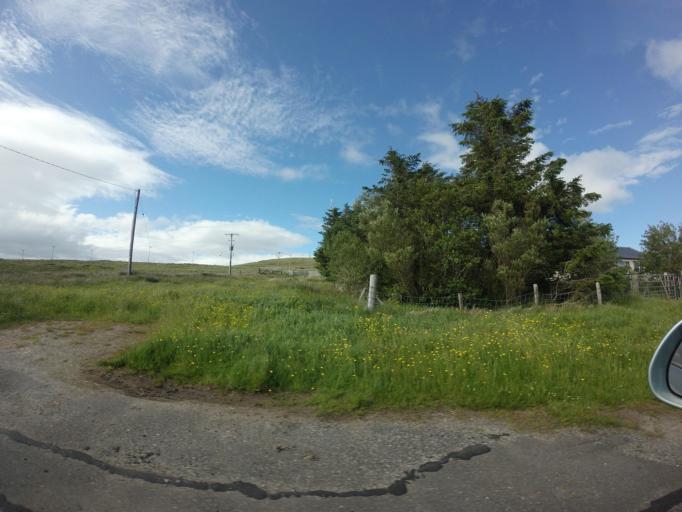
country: GB
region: Scotland
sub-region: Eilean Siar
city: Stornoway
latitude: 58.1722
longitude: -6.5857
